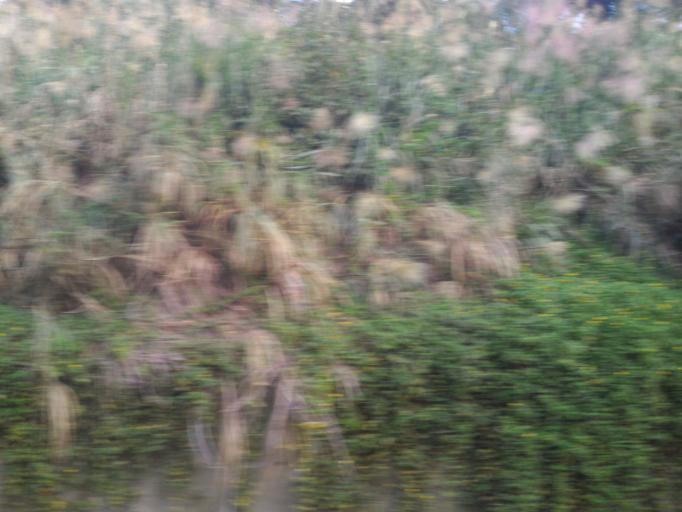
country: TW
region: Taiwan
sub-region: Taoyuan
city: Taoyuan
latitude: 24.9586
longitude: 121.3388
